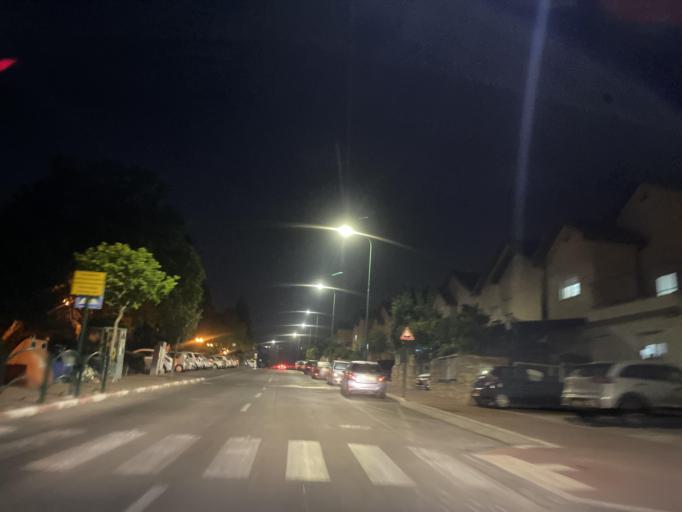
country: IL
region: Haifa
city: Daliyat el Karmil
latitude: 32.6470
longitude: 35.0903
